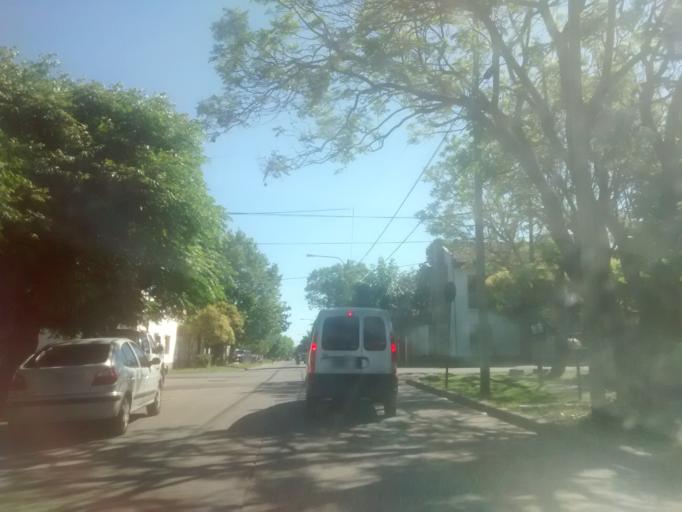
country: AR
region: Buenos Aires
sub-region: Partido de La Plata
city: La Plata
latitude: -34.9401
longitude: -57.9337
